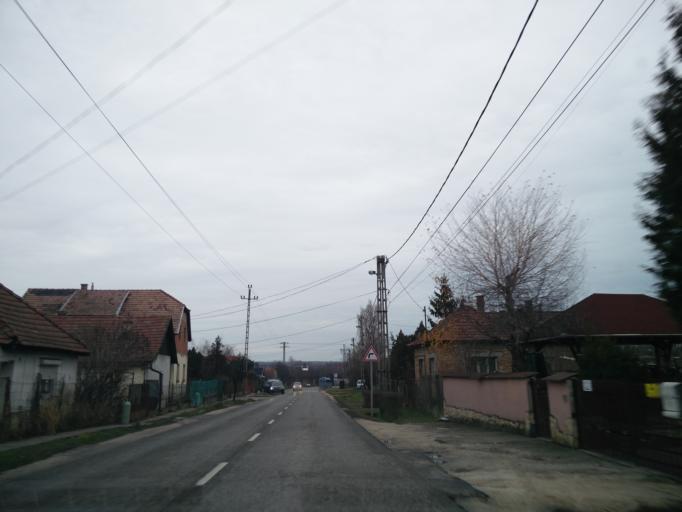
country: HU
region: Pest
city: Gyomro
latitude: 47.4131
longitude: 19.3890
